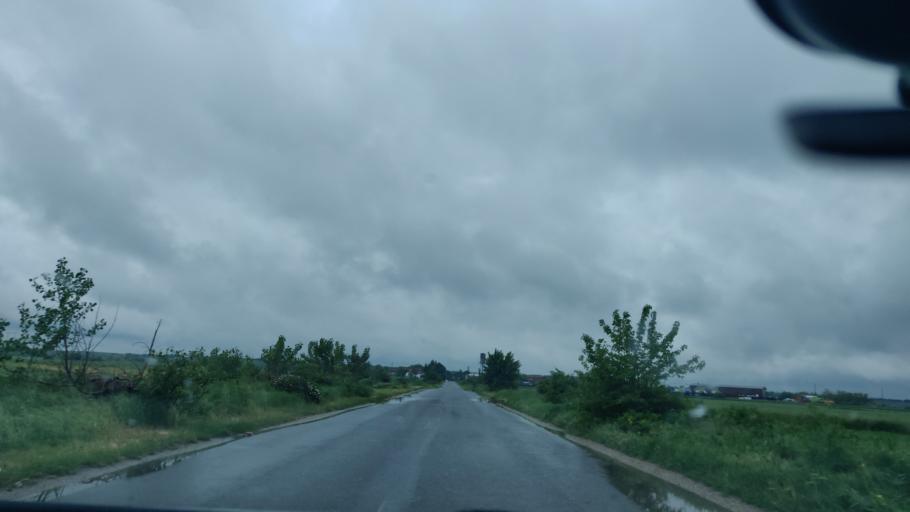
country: RO
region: Giurgiu
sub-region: Comuna Bulbucata
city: Bulbucata
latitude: 44.2720
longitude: 25.8365
